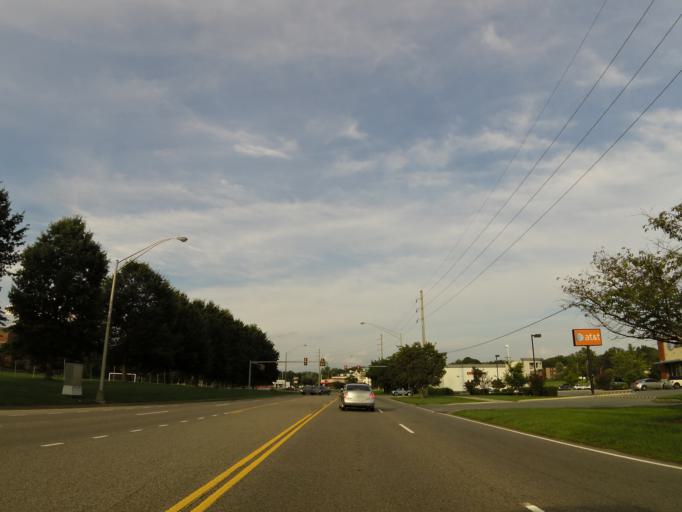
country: US
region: Tennessee
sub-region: Anderson County
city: Oak Ridge
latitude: 36.0149
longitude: -84.2543
